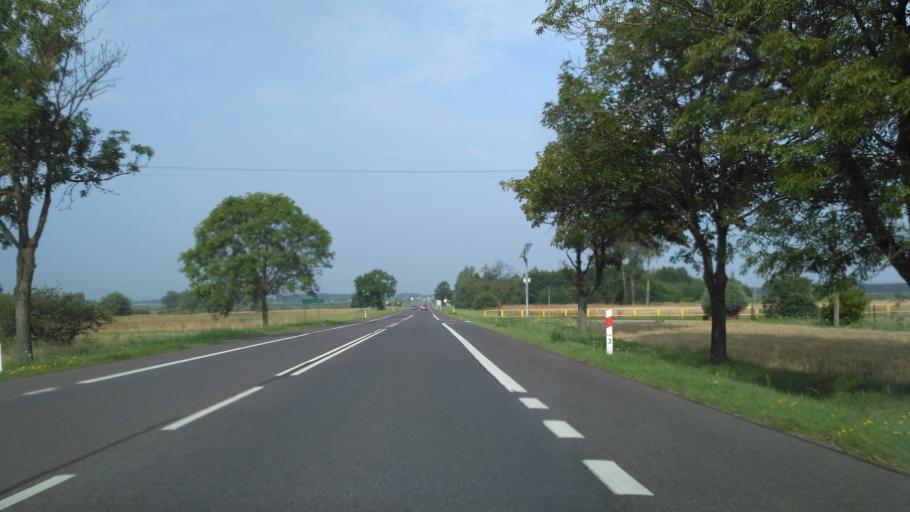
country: PL
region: Lublin Voivodeship
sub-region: Powiat swidnicki
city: Trawniki
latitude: 51.1658
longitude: 23.0598
